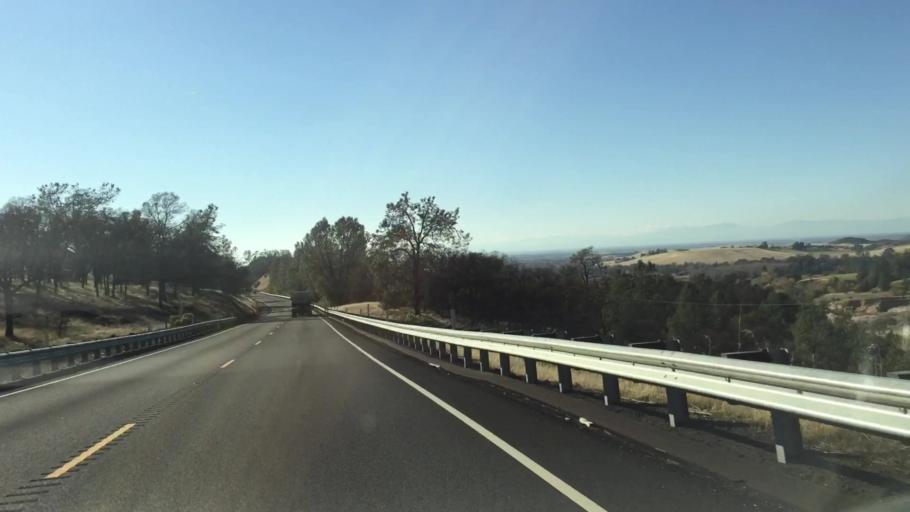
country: US
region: California
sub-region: Butte County
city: Paradise
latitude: 39.6460
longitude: -121.5656
